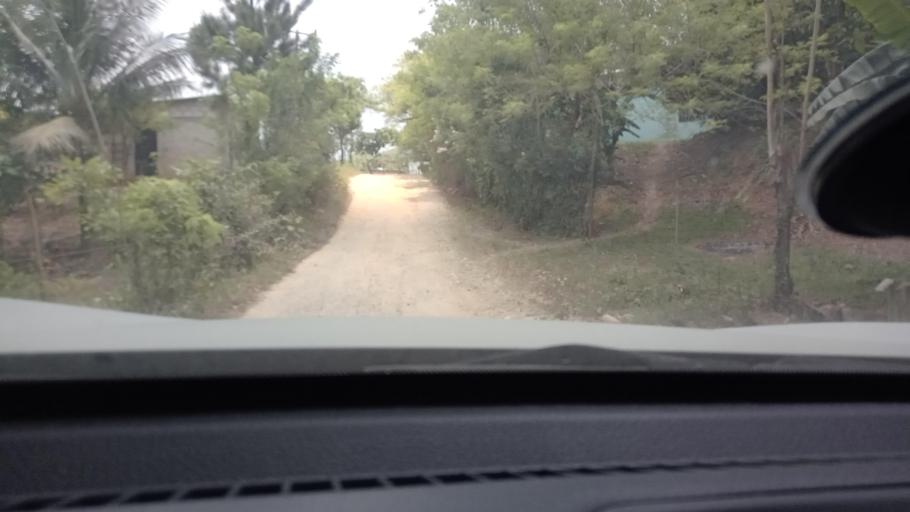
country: MX
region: Tabasco
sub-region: Huimanguillo
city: Francisco Rueda
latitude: 17.5211
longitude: -93.8859
